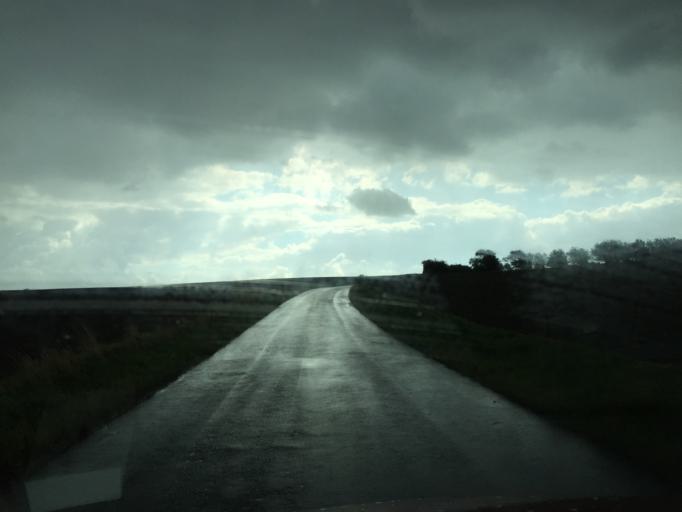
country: DK
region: South Denmark
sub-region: Sonderborg Kommune
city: Dybbol
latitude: 54.9661
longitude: 9.7267
